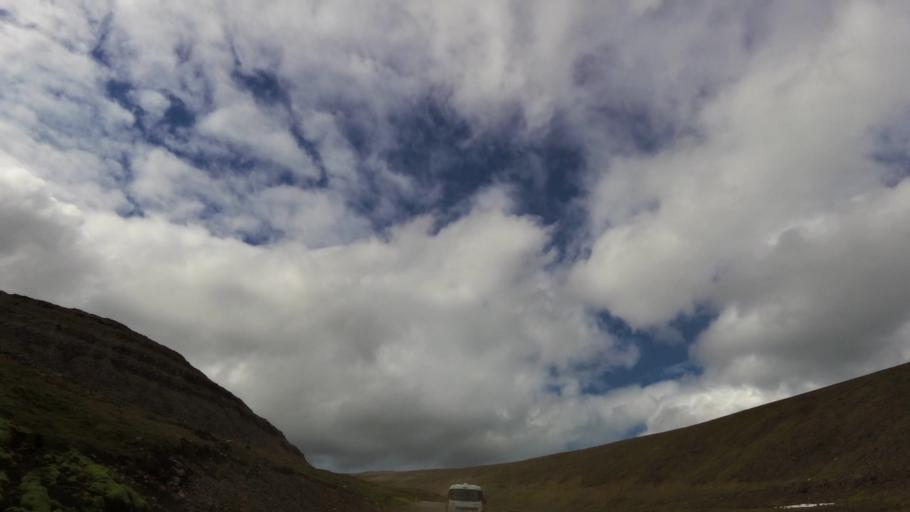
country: IS
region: Westfjords
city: Isafjoerdur
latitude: 66.1694
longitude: -23.3483
